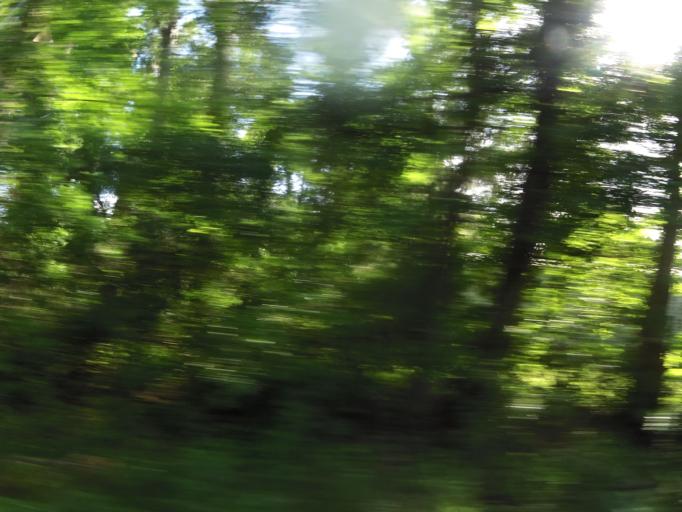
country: US
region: Florida
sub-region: Nassau County
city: Nassau Village-Ratliff
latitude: 30.4669
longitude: -81.8364
